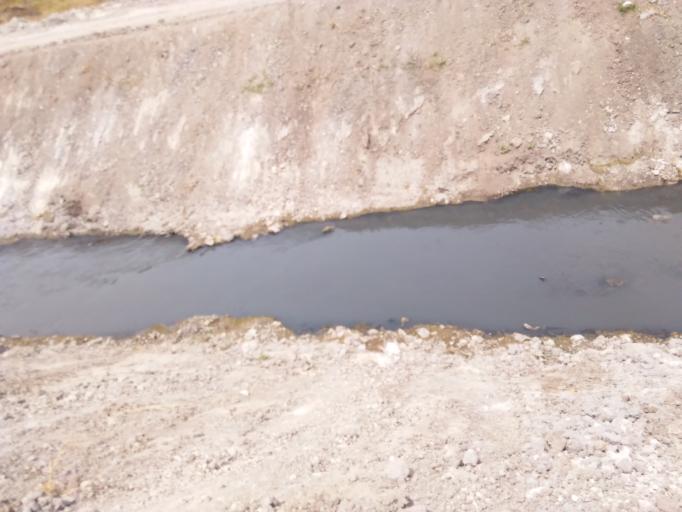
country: MX
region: Nayarit
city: Tepic
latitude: 21.4865
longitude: -104.8496
